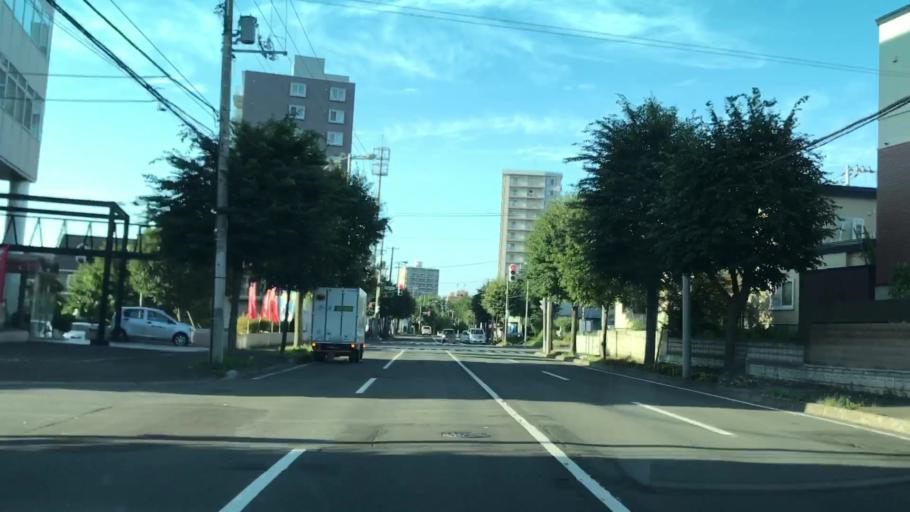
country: JP
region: Hokkaido
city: Sapporo
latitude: 43.0439
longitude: 141.3639
